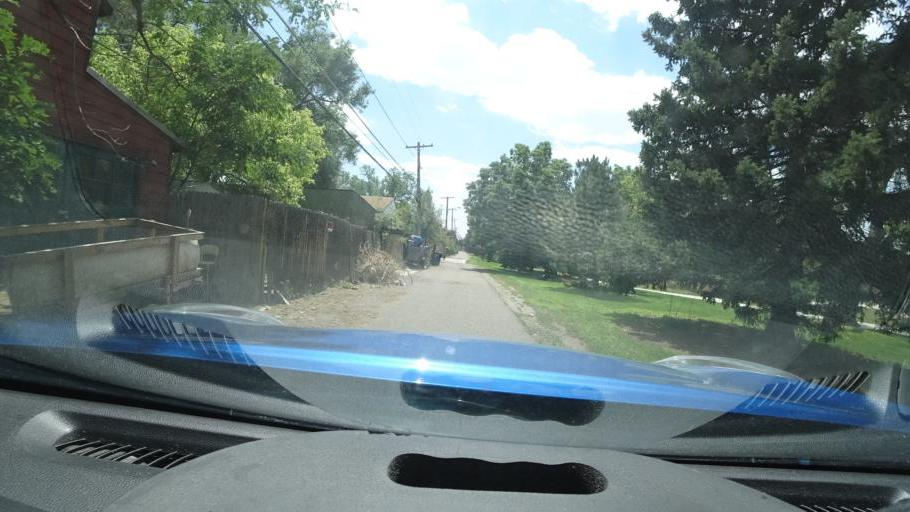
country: US
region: Colorado
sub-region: Arapahoe County
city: Englewood
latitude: 39.6753
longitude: -104.9966
